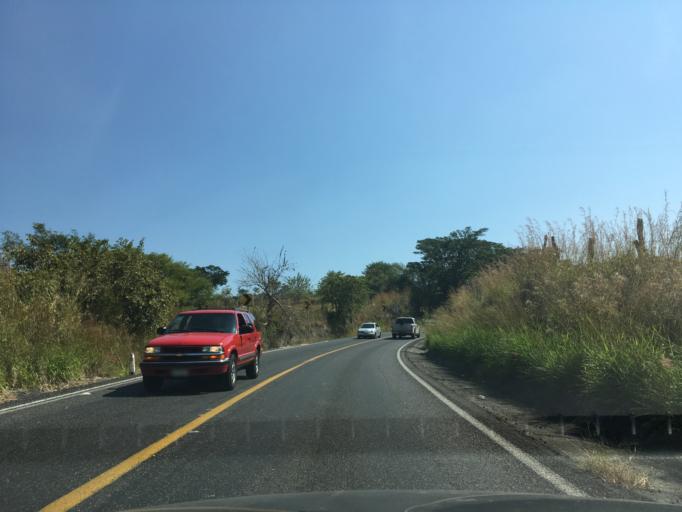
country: MX
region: Michoacan
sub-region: Gabriel Zamora
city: Lombardia
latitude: 19.2232
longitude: -102.0464
